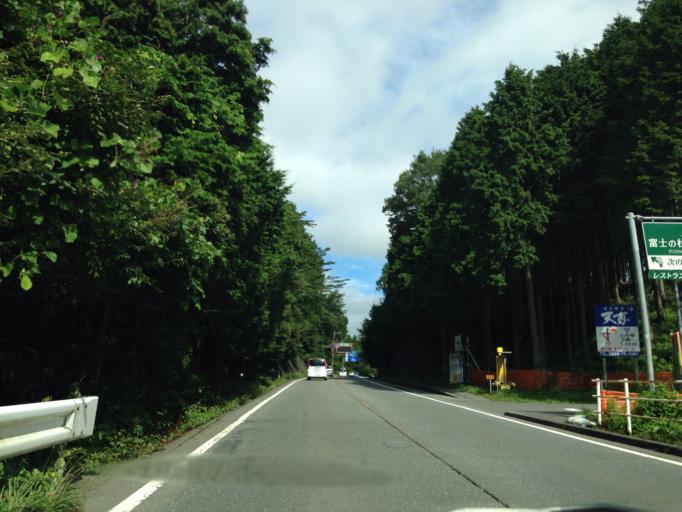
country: JP
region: Shizuoka
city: Gotemba
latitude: 35.3498
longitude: 138.8770
